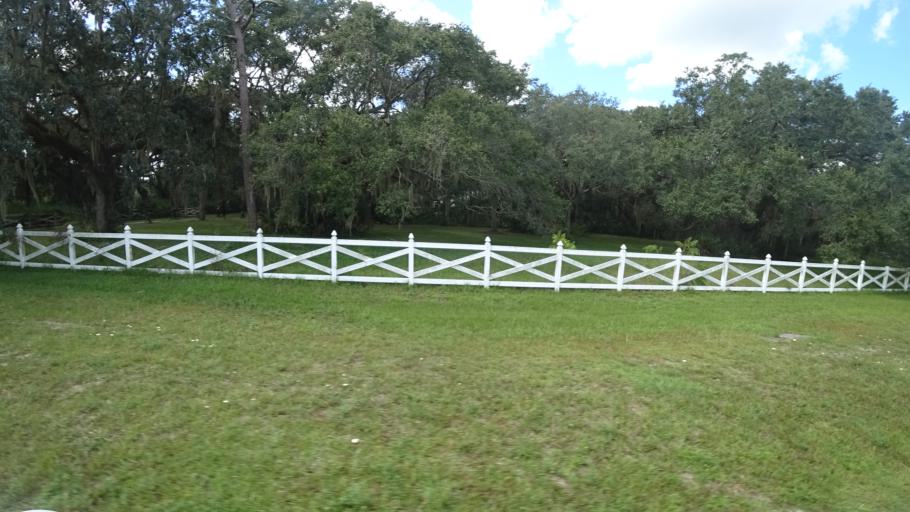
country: US
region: Florida
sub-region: Sarasota County
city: Lake Sarasota
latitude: 27.2873
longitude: -82.2303
